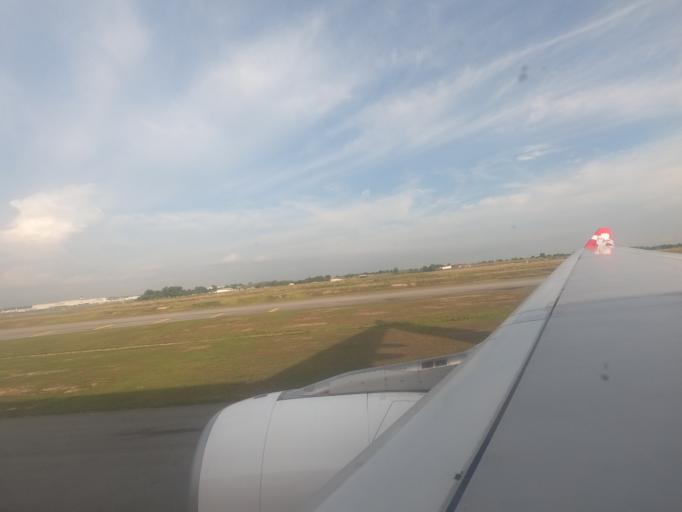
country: MY
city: Sungai Pelek New Village
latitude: 2.7400
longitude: 101.6926
